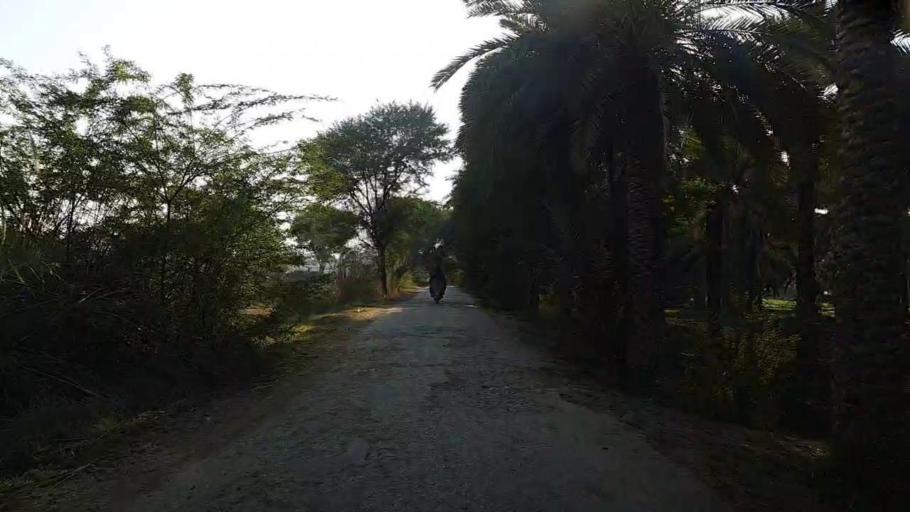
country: PK
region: Sindh
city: Ranipur
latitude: 27.2428
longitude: 68.5371
